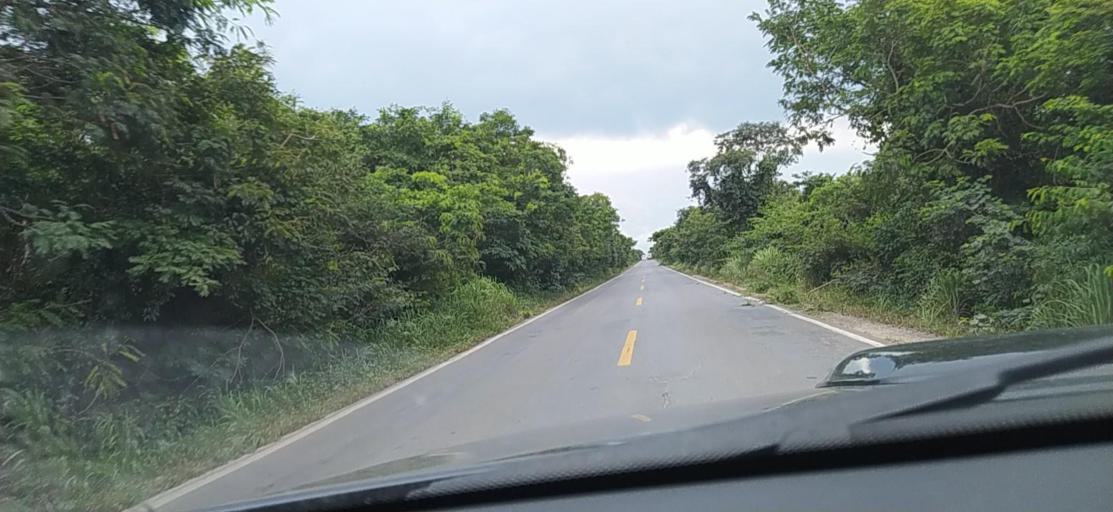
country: BR
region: Minas Gerais
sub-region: Francisco Sa
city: Francisco Sa
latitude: -16.2441
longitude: -43.6258
